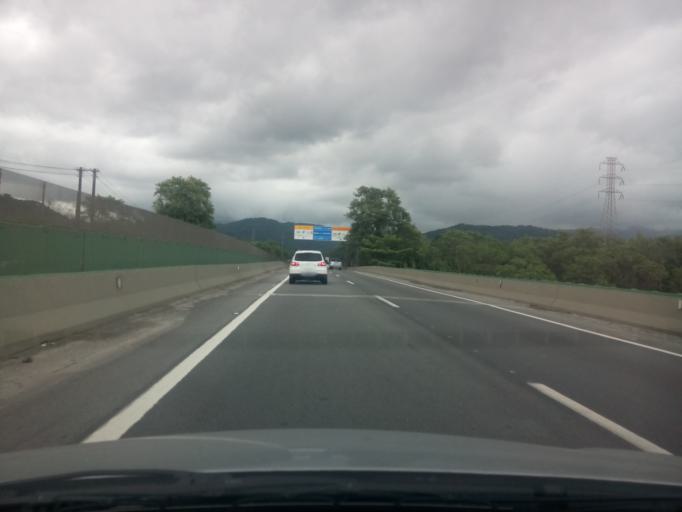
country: BR
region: Sao Paulo
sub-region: Santos
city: Santos
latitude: -23.9028
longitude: -46.2973
